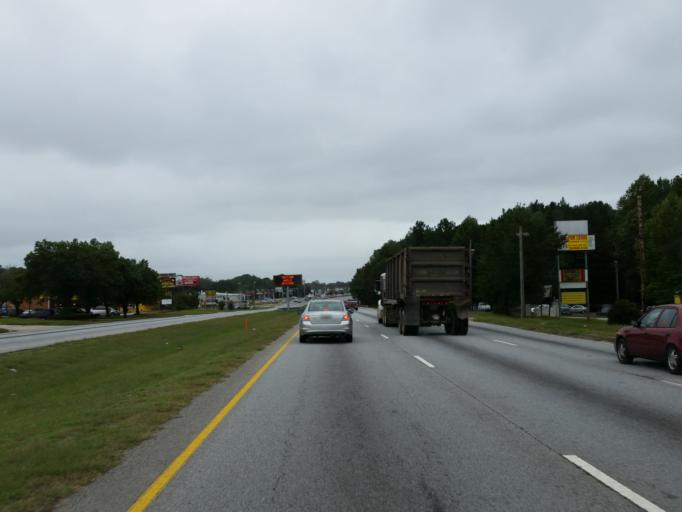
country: US
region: Georgia
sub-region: Clayton County
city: Morrow
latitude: 33.5818
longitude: -84.3767
